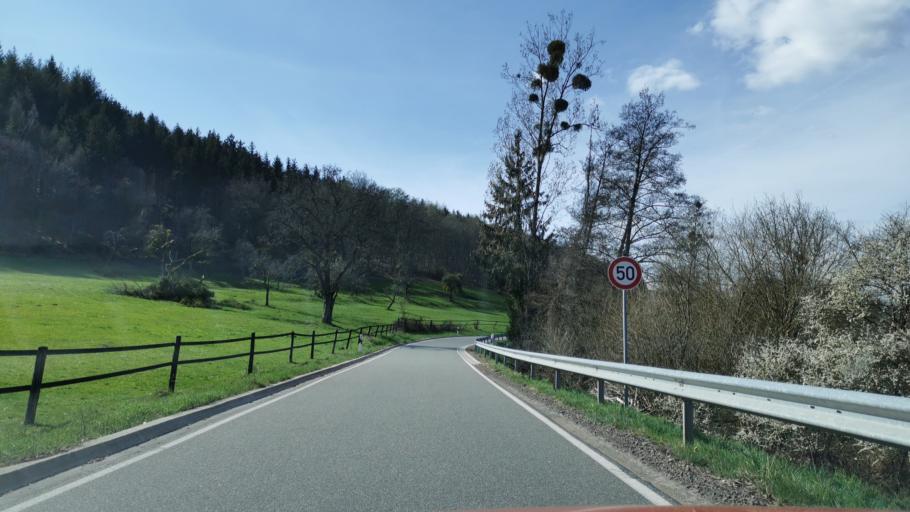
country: DE
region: Rheinland-Pfalz
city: Dreis
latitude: 49.9284
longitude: 6.8288
